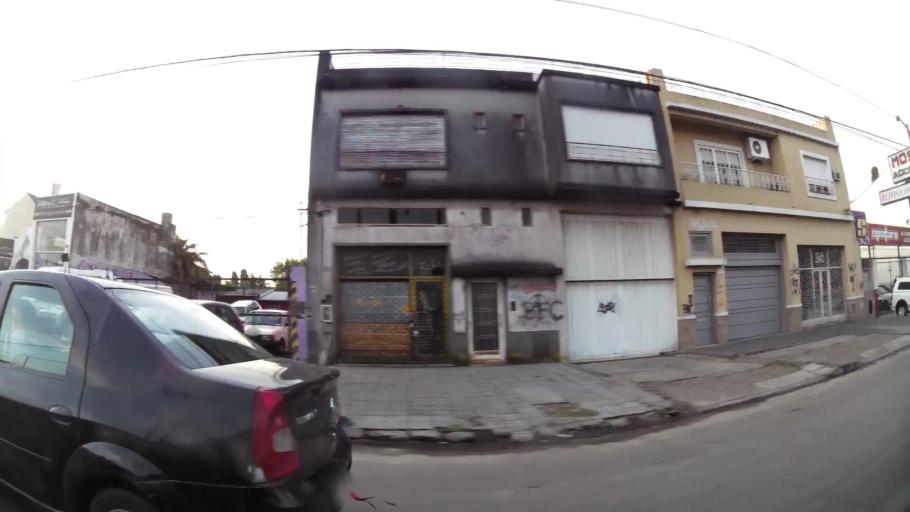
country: AR
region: Buenos Aires
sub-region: Partido de Lomas de Zamora
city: Lomas de Zamora
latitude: -34.7687
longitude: -58.3761
